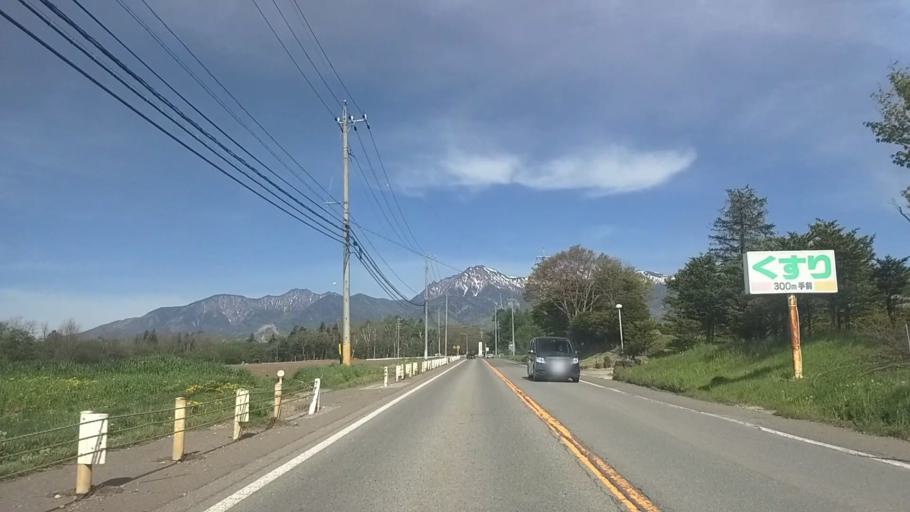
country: JP
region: Yamanashi
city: Nirasaki
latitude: 35.9564
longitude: 138.4673
